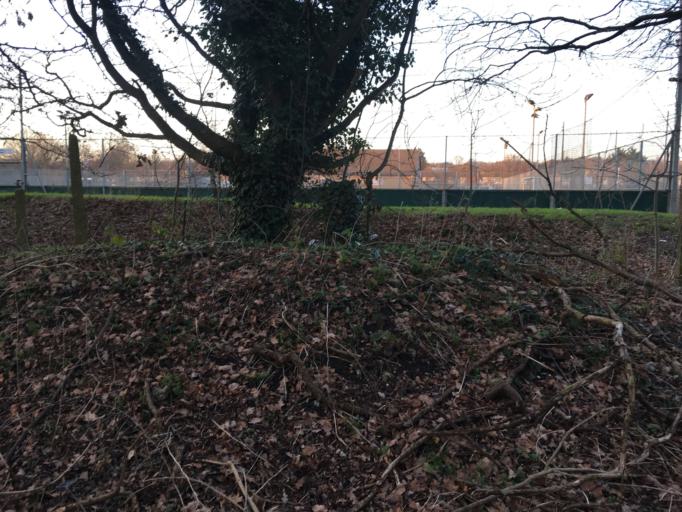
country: GB
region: England
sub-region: Greater London
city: Hendon
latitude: 51.6069
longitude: -0.2258
